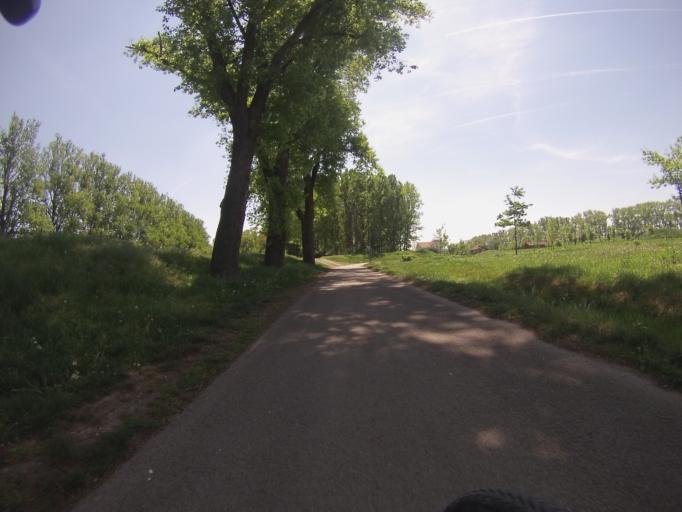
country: CZ
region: South Moravian
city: Zidlochovice
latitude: 49.0268
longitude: 16.6229
